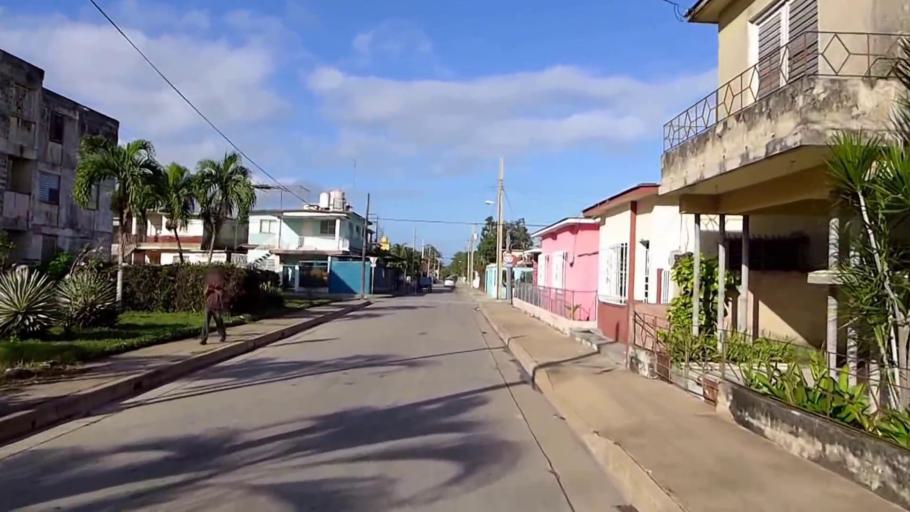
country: CU
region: Camaguey
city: Camaguey
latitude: 21.3864
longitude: -77.9217
